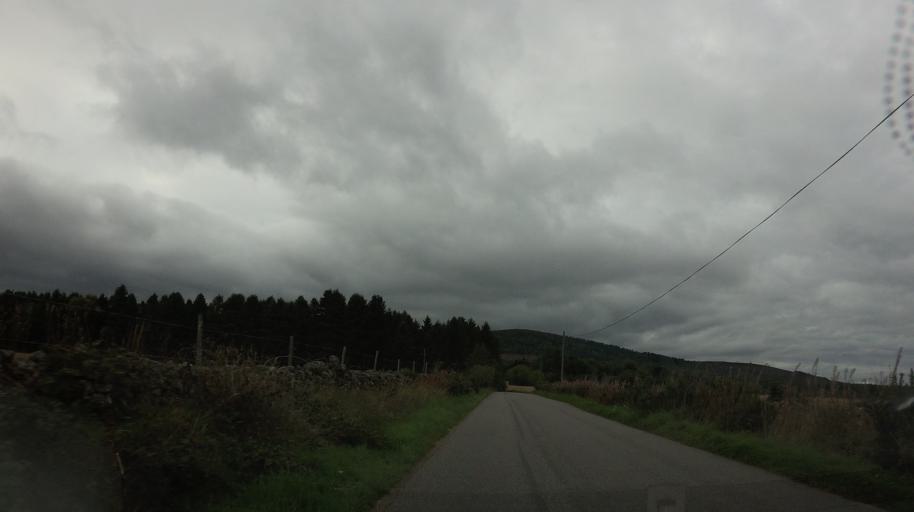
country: GB
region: Scotland
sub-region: Aberdeenshire
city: Banchory
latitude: 57.0947
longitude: -2.4479
